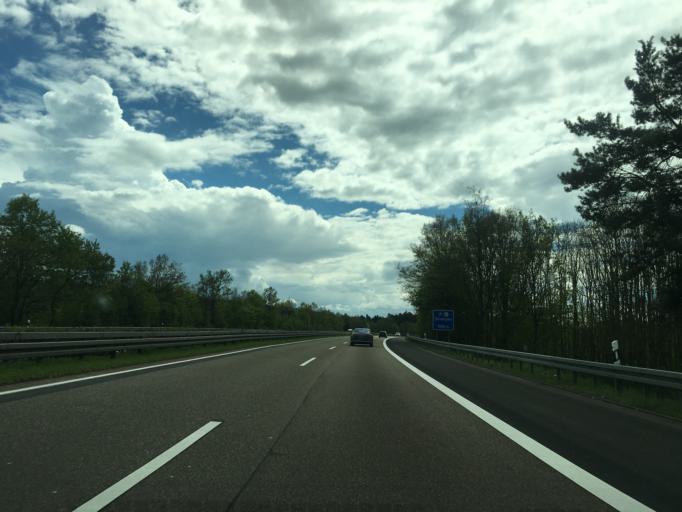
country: DE
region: Hesse
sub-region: Regierungsbezirk Kassel
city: Kirchheim
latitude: 50.7934
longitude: 9.5477
